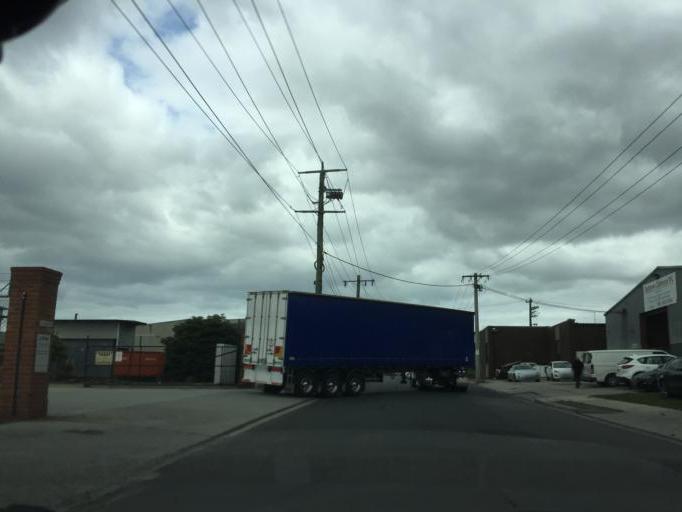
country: AU
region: Victoria
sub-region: Brimbank
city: Brooklyn
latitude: -37.8062
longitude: 144.8520
